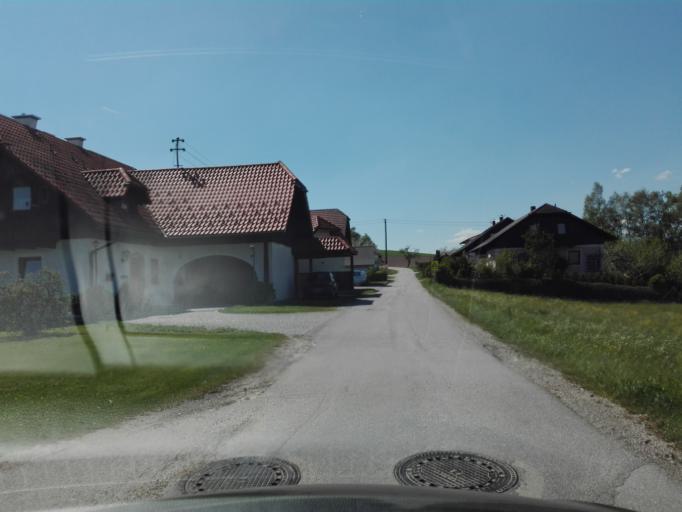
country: AT
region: Upper Austria
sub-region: Politischer Bezirk Urfahr-Umgebung
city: Feldkirchen an der Donau
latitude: 48.3459
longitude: 13.9563
